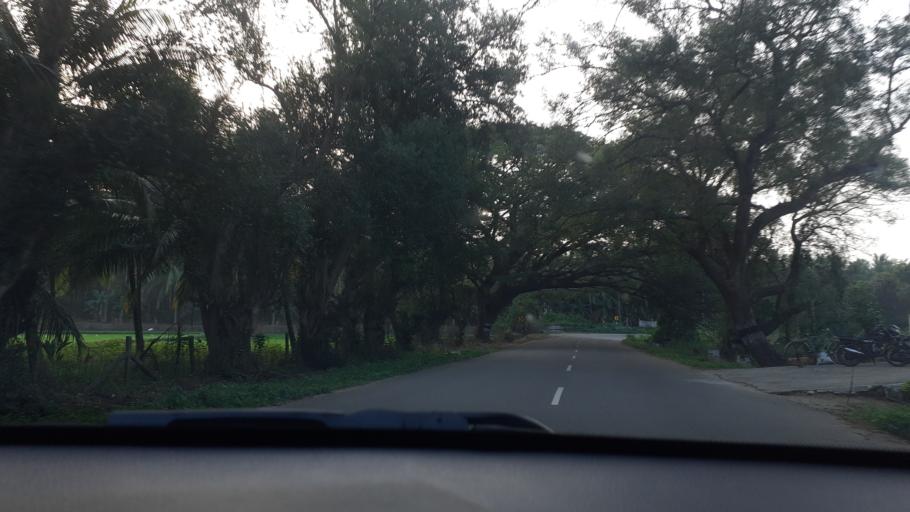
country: IN
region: Tamil Nadu
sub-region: Dindigul
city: Ayakudi
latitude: 10.4175
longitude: 77.5361
